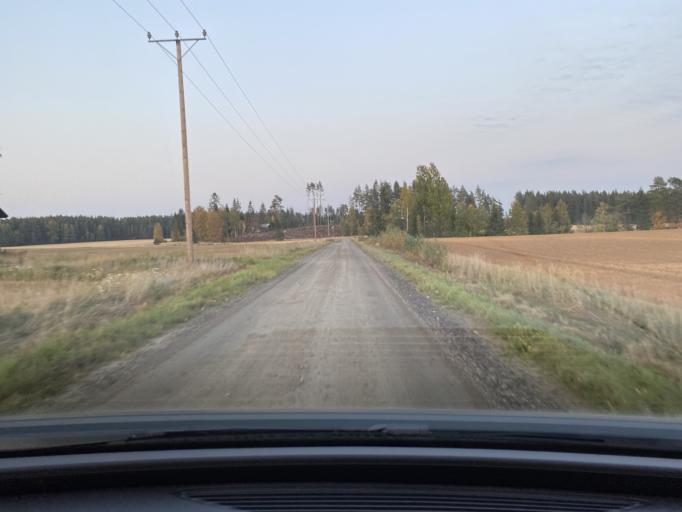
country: FI
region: Pirkanmaa
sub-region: Lounais-Pirkanmaa
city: Punkalaidun
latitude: 61.1067
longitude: 23.2204
